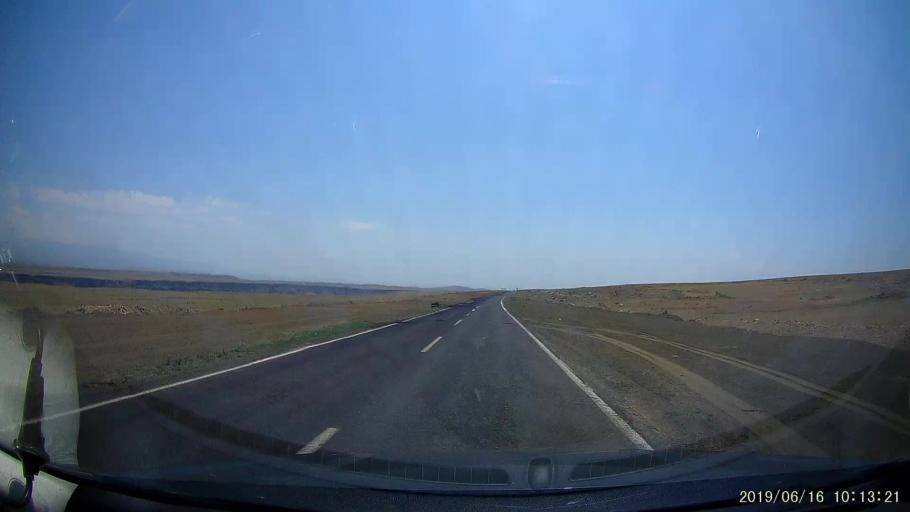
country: TR
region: Igdir
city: Tuzluca
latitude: 40.1928
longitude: 43.6409
